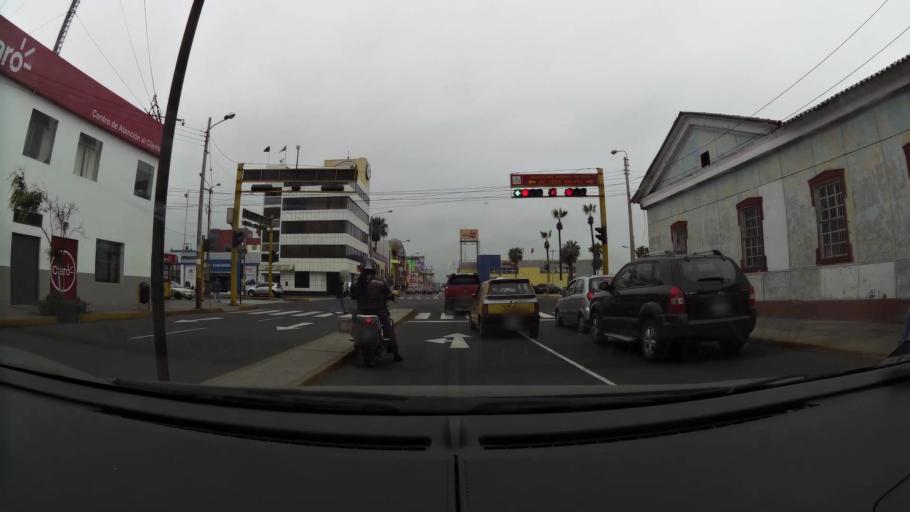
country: PE
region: Ancash
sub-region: Provincia de Santa
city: Chimbote
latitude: -9.0774
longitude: -78.5908
